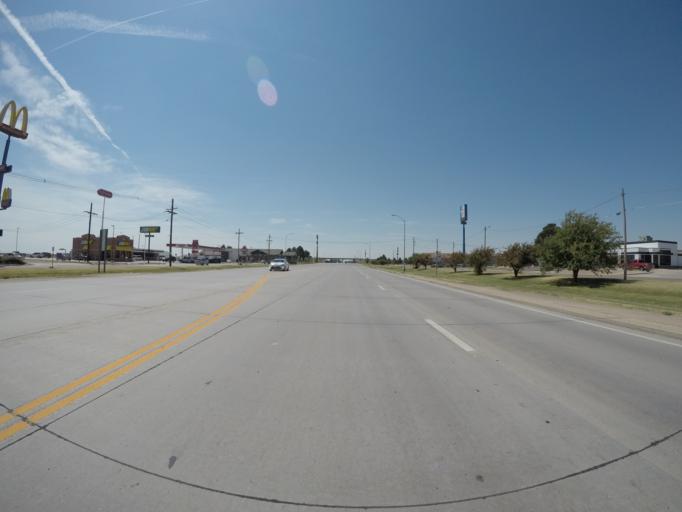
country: US
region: Kansas
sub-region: Sherman County
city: Goodland
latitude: 39.3318
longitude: -101.7264
